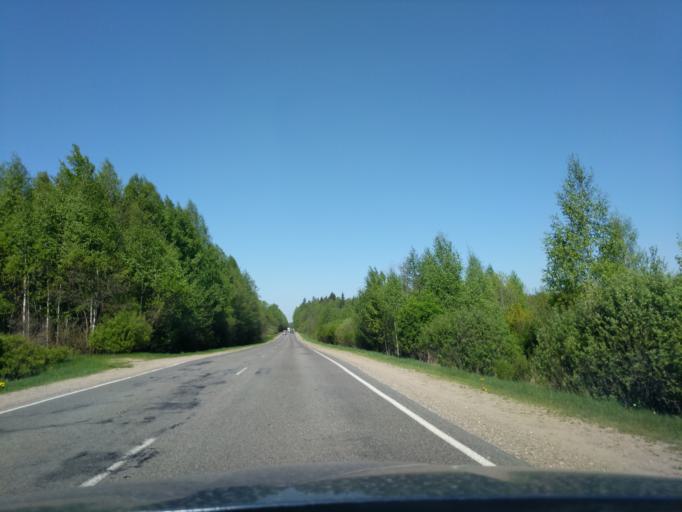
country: BY
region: Minsk
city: Il'ya
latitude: 54.3997
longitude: 27.3304
